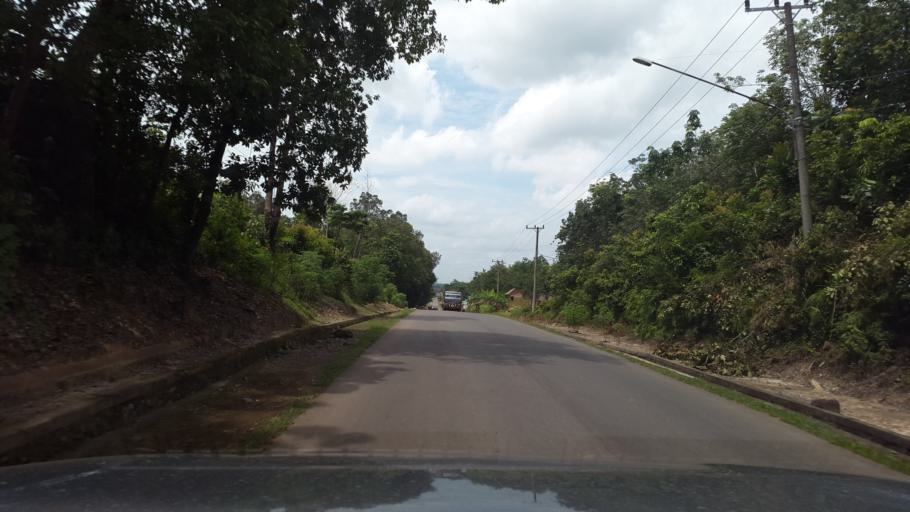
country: ID
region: South Sumatra
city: Gunungmegang Dalam
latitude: -3.3144
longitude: 103.8905
